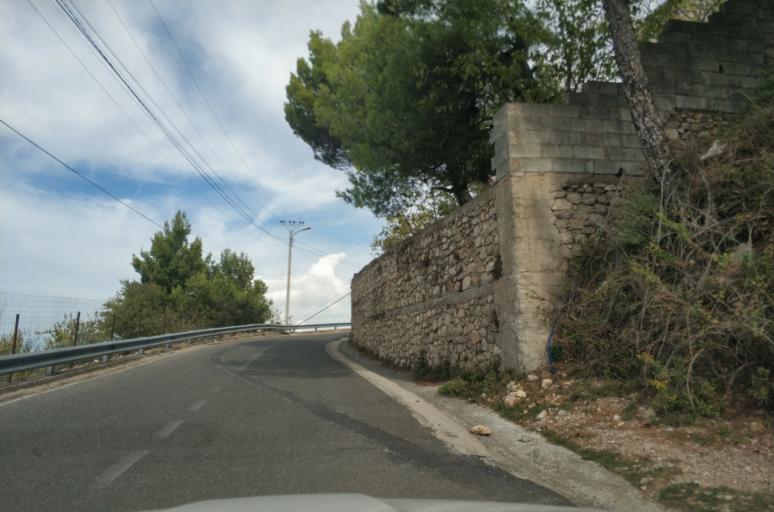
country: AL
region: Durres
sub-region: Rrethi i Krujes
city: Kruje
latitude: 41.5158
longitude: 19.7937
